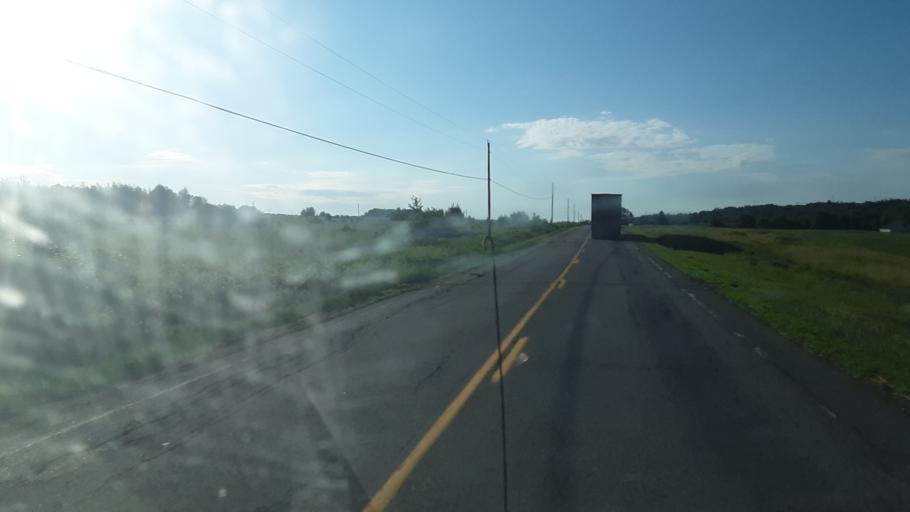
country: US
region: Maine
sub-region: Penobscot County
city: Patten
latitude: 46.1369
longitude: -68.1907
